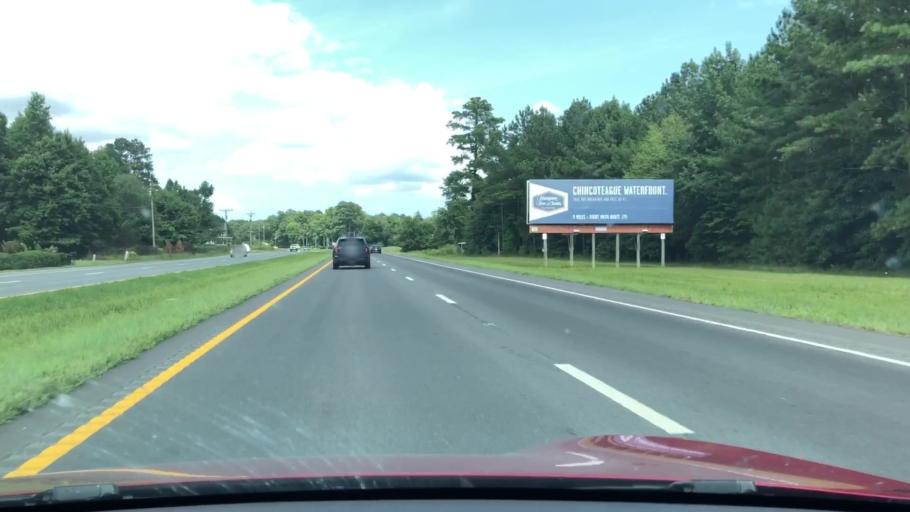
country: US
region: Virginia
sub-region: Accomack County
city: Accomac
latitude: 37.8243
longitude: -75.5826
